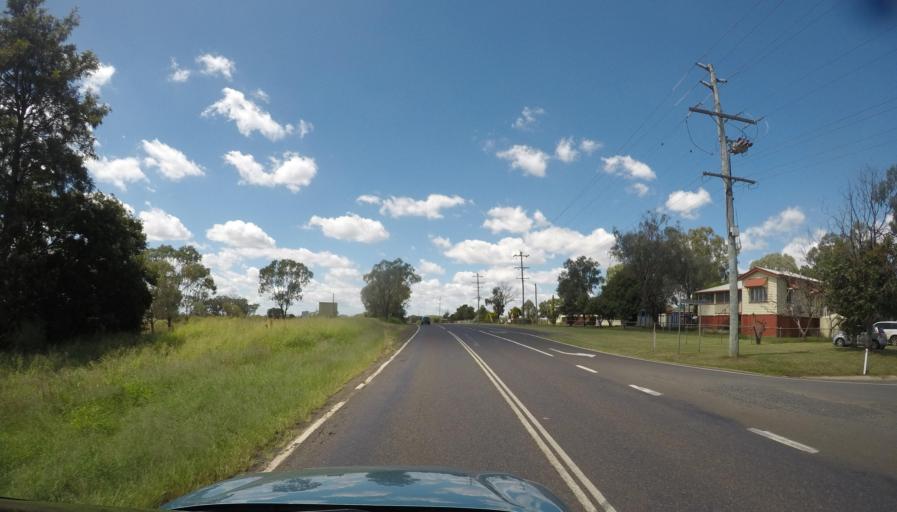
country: AU
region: Queensland
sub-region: Toowoomba
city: Oakey
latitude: -27.5538
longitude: 151.6964
